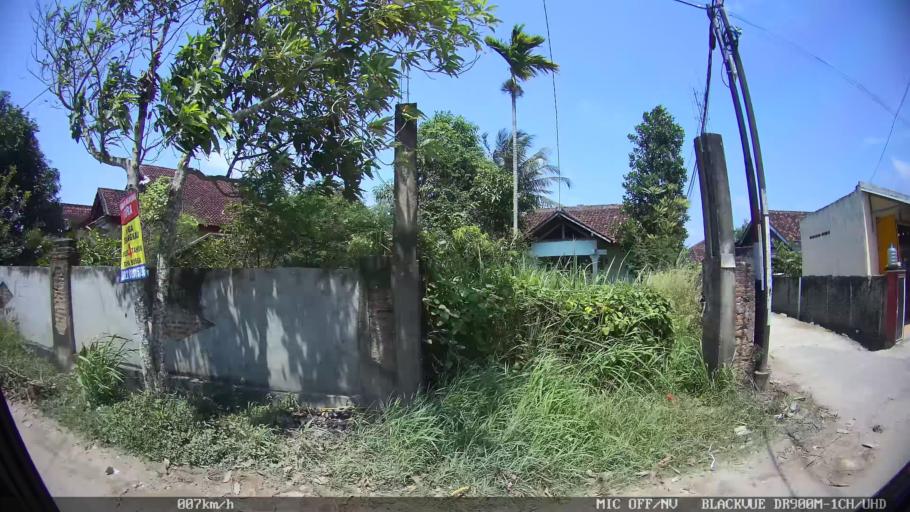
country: ID
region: Lampung
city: Kedaton
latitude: -5.3563
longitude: 105.2767
